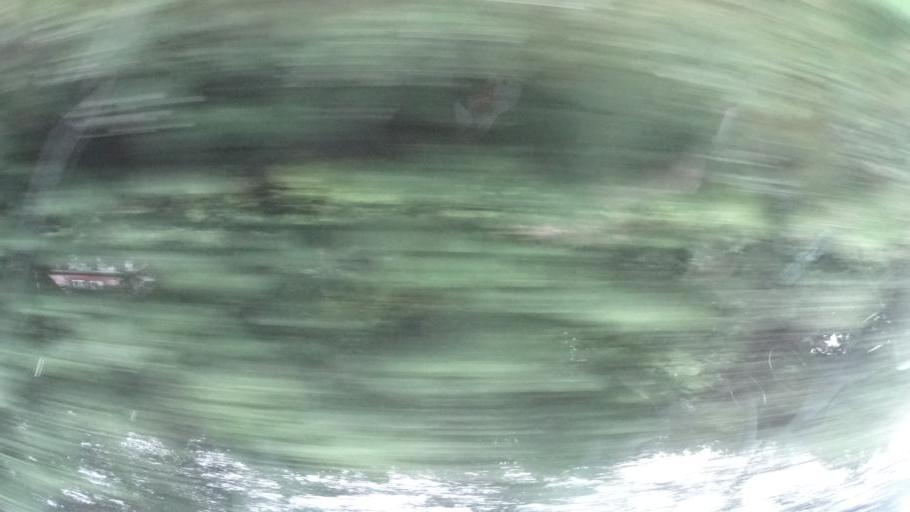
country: DE
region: Lower Saxony
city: Pegestorf
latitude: 51.9421
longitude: 9.5123
